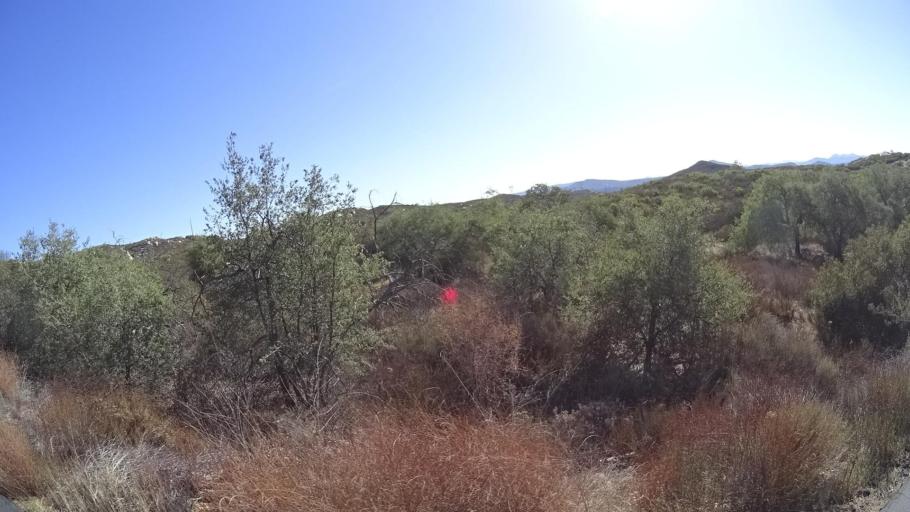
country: MX
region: Baja California
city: Tecate
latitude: 32.6700
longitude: -116.7079
